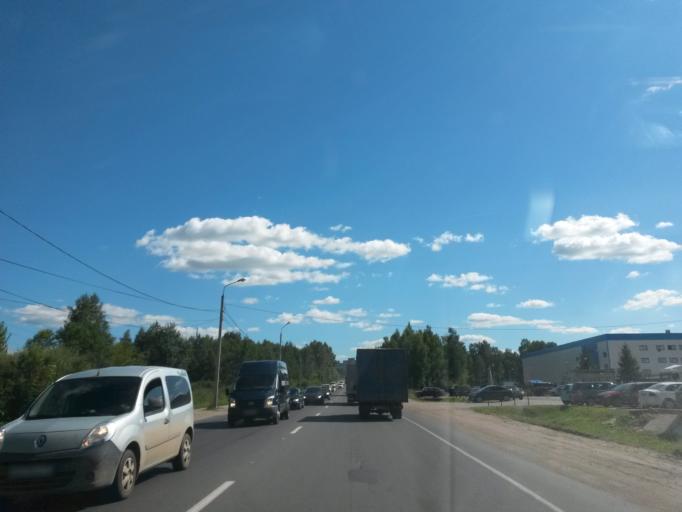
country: RU
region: Jaroslavl
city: Yaroslavl
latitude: 57.5937
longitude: 39.8134
